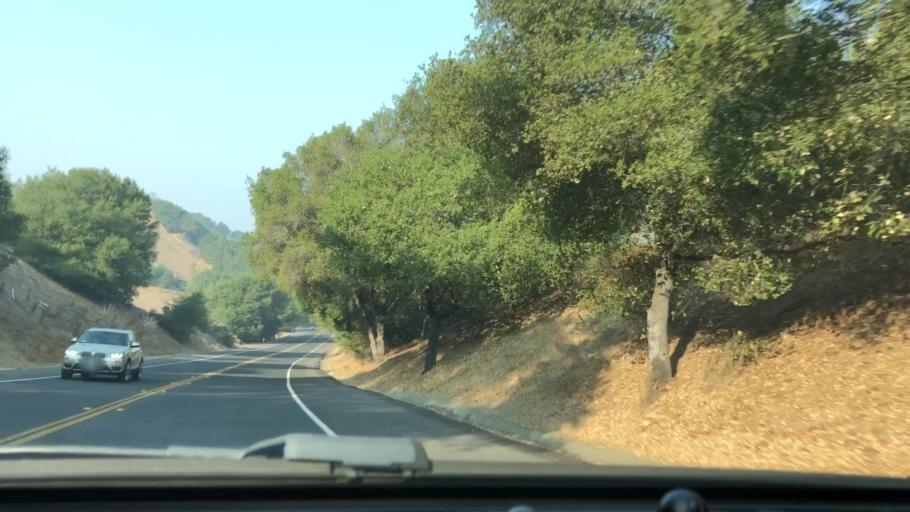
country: US
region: California
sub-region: Contra Costa County
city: Orinda
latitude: 37.9193
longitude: -122.1853
